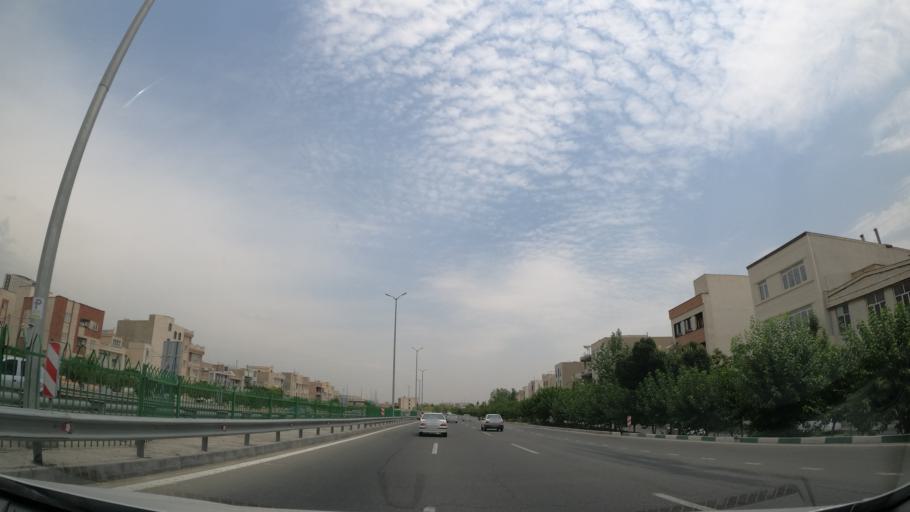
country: IR
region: Tehran
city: Shahr-e Qods
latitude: 35.7388
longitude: 51.2617
